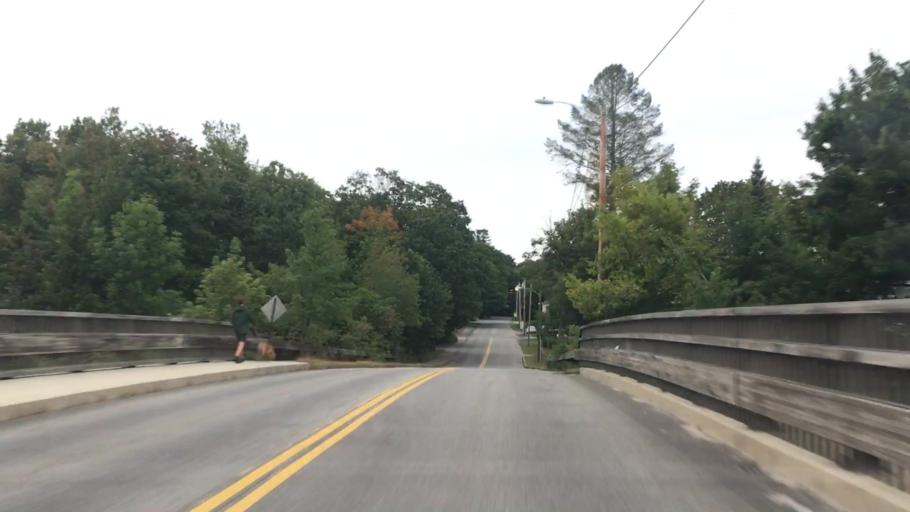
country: US
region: Maine
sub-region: Cumberland County
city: Brunswick
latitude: 43.9109
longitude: -69.9717
